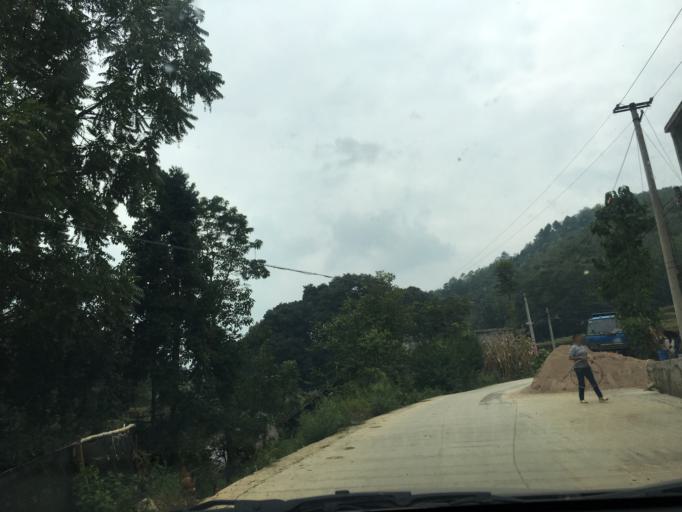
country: CN
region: Guangxi Zhuangzu Zizhiqu
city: Xinzhou
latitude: 25.5433
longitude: 105.5791
